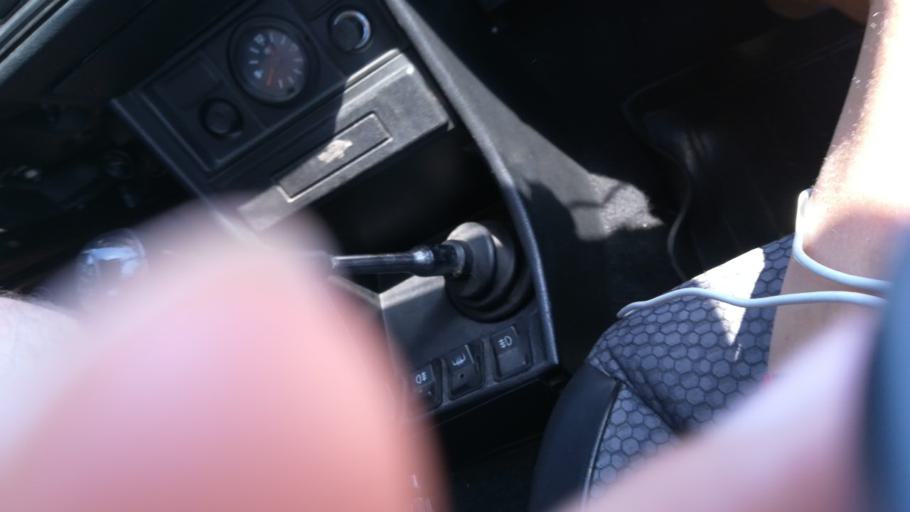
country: RU
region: Krasnodarskiy
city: Vityazevo
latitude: 44.9889
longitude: 37.2483
